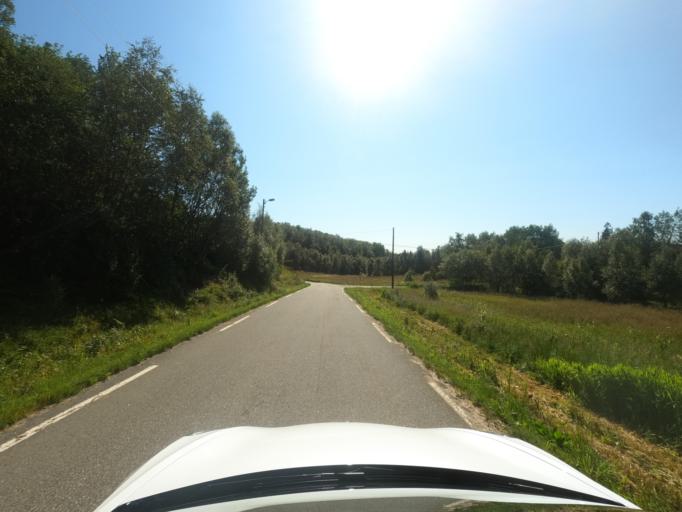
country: NO
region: Nordland
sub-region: Hadsel
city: Stokmarknes
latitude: 68.3036
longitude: 15.0948
